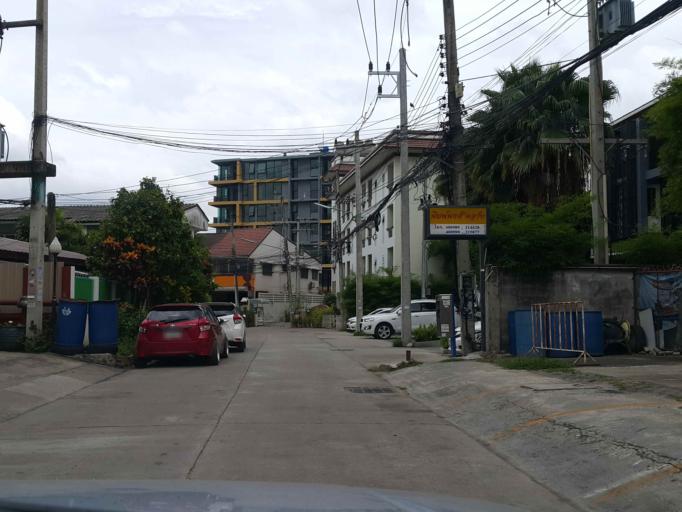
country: TH
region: Chiang Mai
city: Chiang Mai
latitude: 18.8003
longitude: 98.9654
